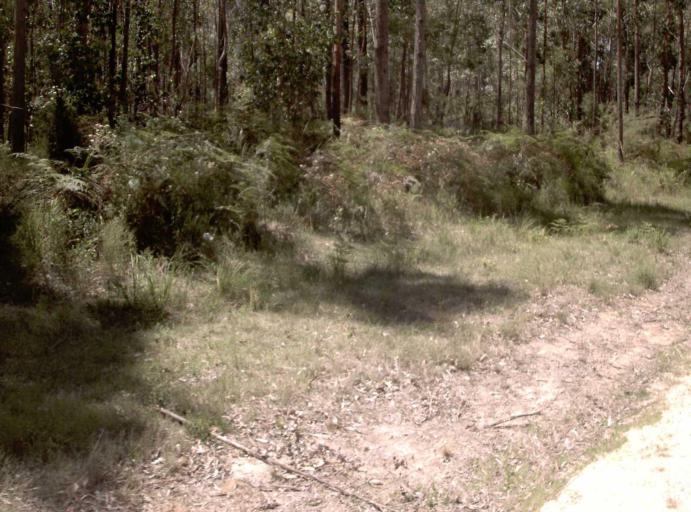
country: AU
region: Victoria
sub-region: East Gippsland
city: Lakes Entrance
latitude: -37.6865
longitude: 148.7592
